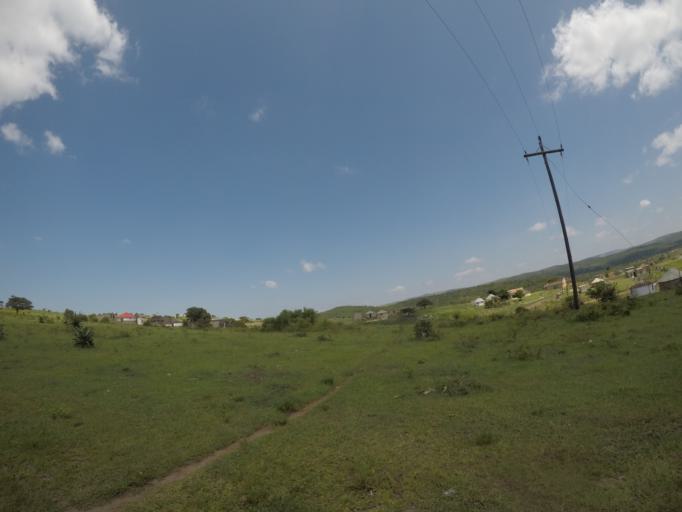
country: ZA
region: KwaZulu-Natal
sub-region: uThungulu District Municipality
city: Empangeni
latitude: -28.6000
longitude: 31.7344
